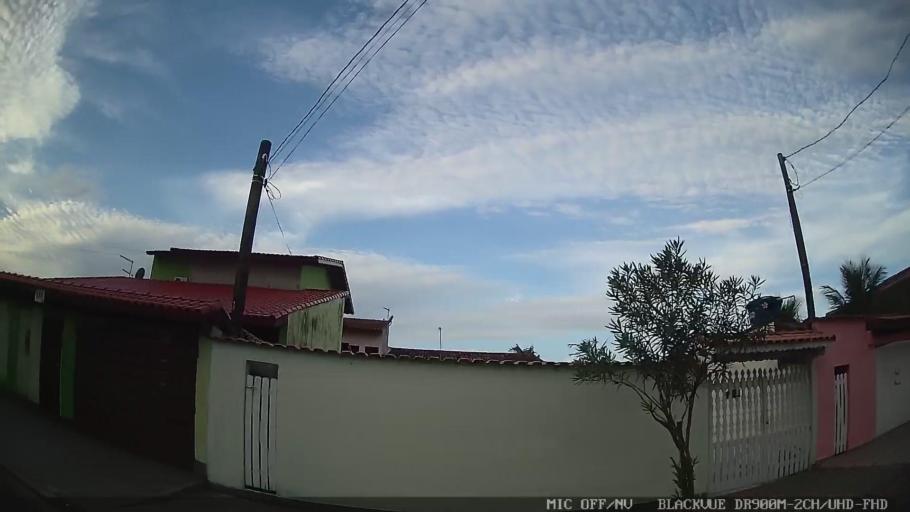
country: BR
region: Sao Paulo
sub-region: Itanhaem
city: Itanhaem
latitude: -24.1687
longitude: -46.7746
